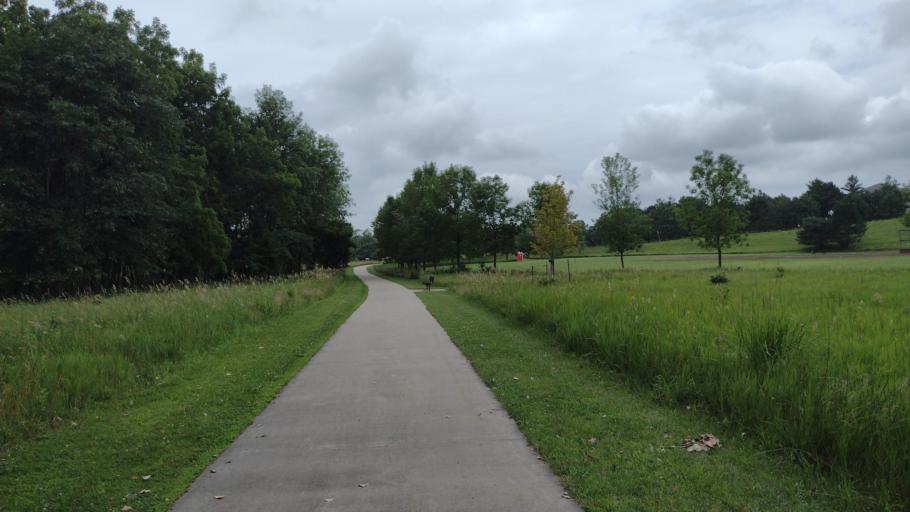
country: US
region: Nebraska
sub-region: Sarpy County
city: Chalco
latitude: 41.1702
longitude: -96.1585
